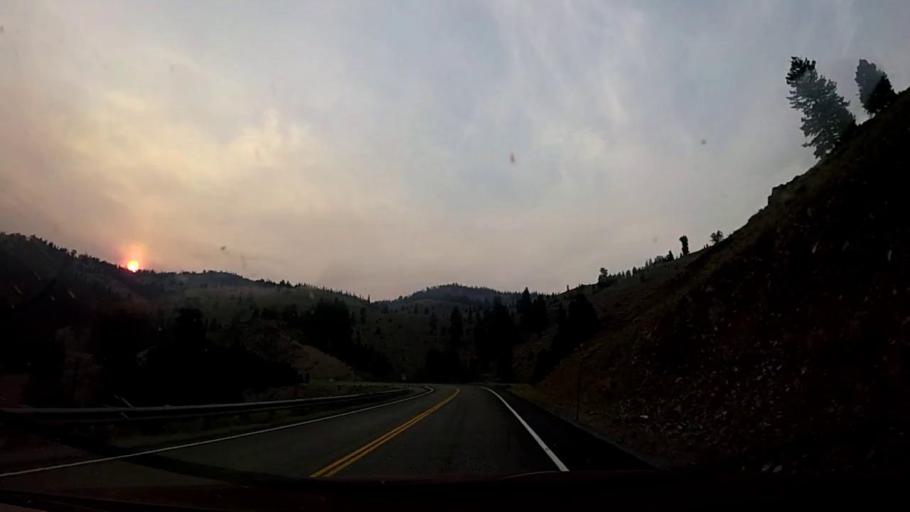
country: US
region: Idaho
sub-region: Blaine County
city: Ketchum
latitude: 43.8861
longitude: -114.6935
